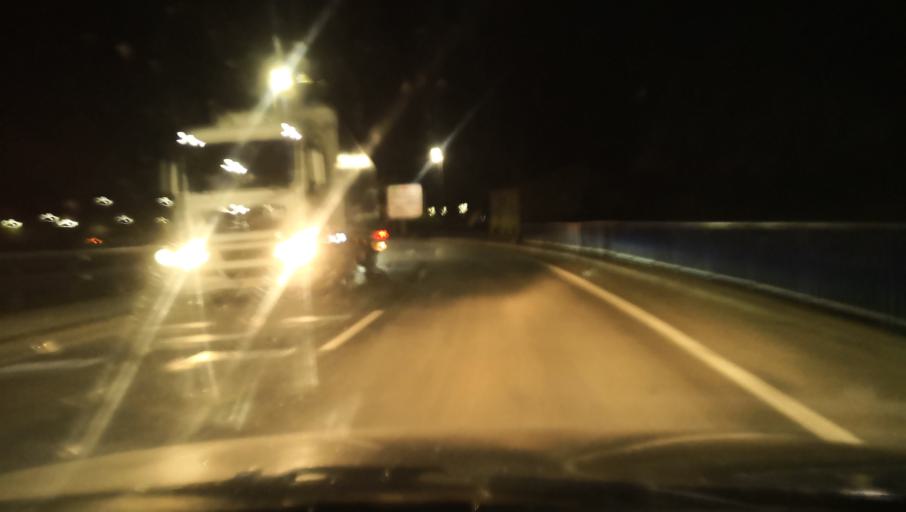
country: ES
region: Castille and Leon
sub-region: Provincia de Zamora
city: Alcanices
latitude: 41.7001
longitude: -6.3494
